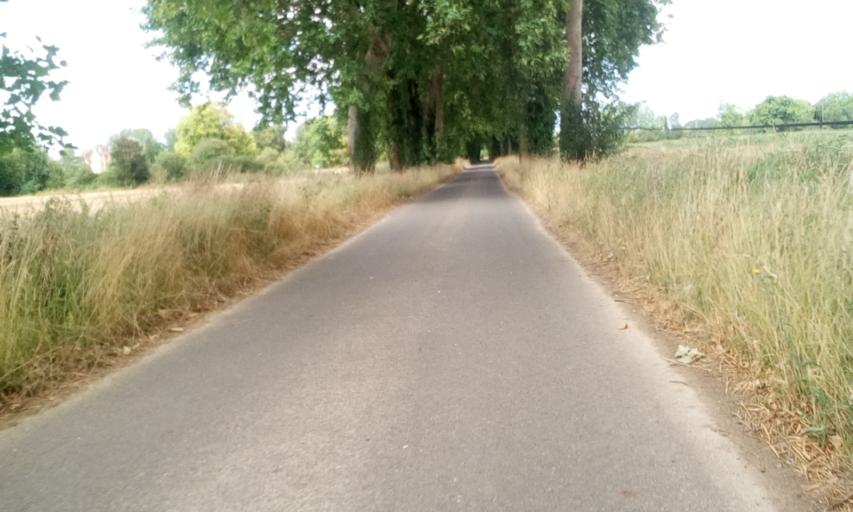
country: FR
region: Lower Normandy
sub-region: Departement du Calvados
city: Bellengreville
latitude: 49.1458
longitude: -0.2074
